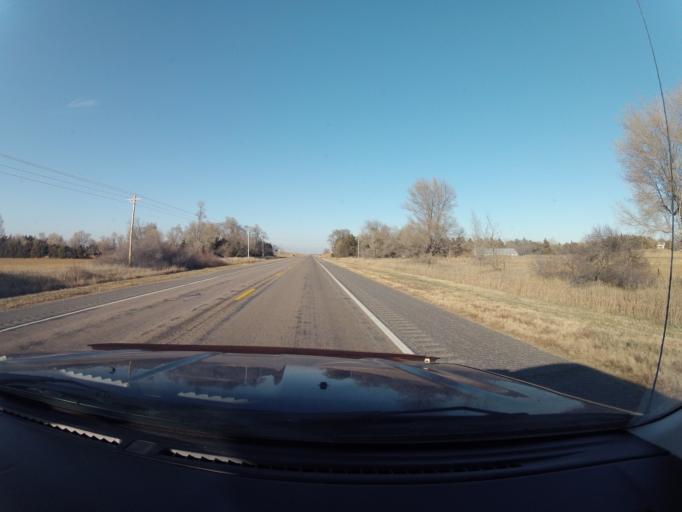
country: US
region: Nebraska
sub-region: Kearney County
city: Minden
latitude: 40.6101
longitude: -98.9516
